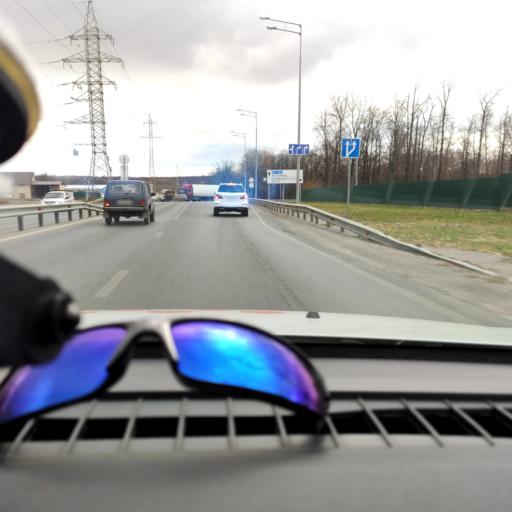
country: RU
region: Samara
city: Novosemeykino
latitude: 53.3486
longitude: 50.2318
